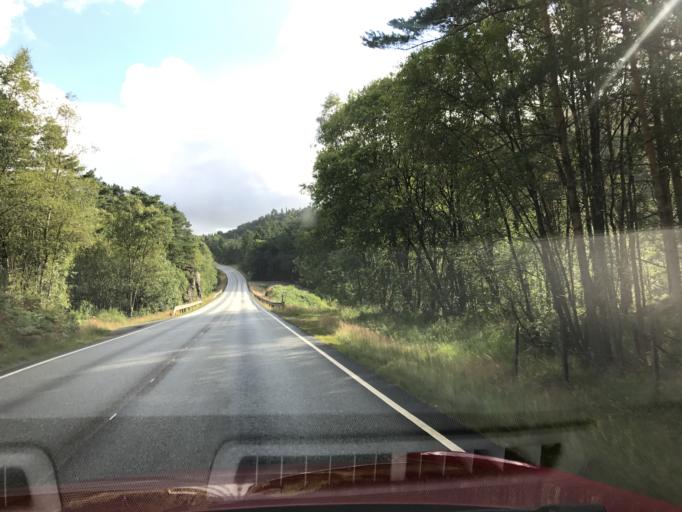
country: NO
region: Hordaland
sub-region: Sveio
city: Sveio
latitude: 59.5954
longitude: 5.4490
